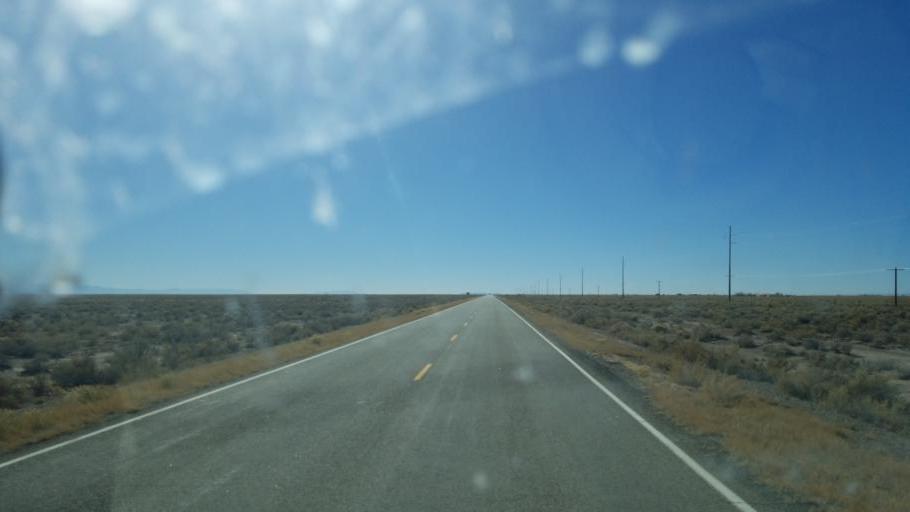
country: US
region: Colorado
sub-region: Saguache County
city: Center
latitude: 37.8668
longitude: -105.8938
